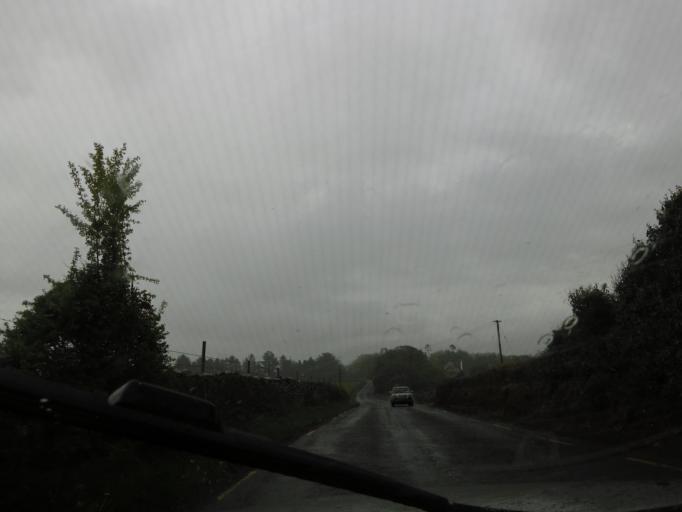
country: IE
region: Connaught
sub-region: Maigh Eo
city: Ballinrobe
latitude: 53.5454
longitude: -9.2721
